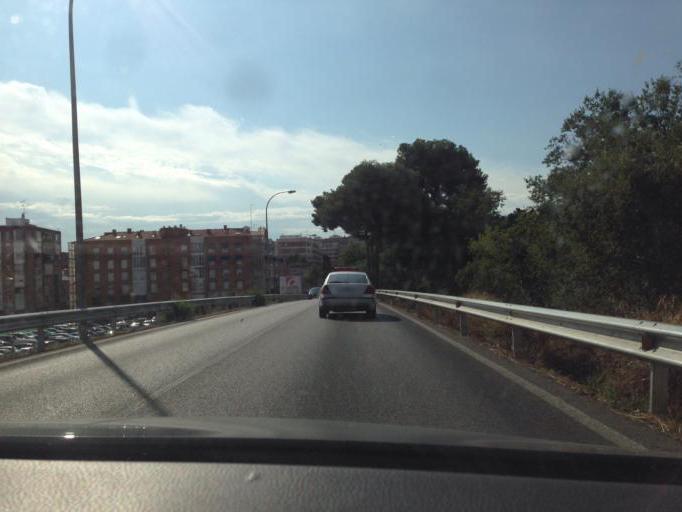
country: ES
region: Madrid
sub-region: Provincia de Madrid
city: Alcala de Henares
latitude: 40.4869
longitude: -3.3721
